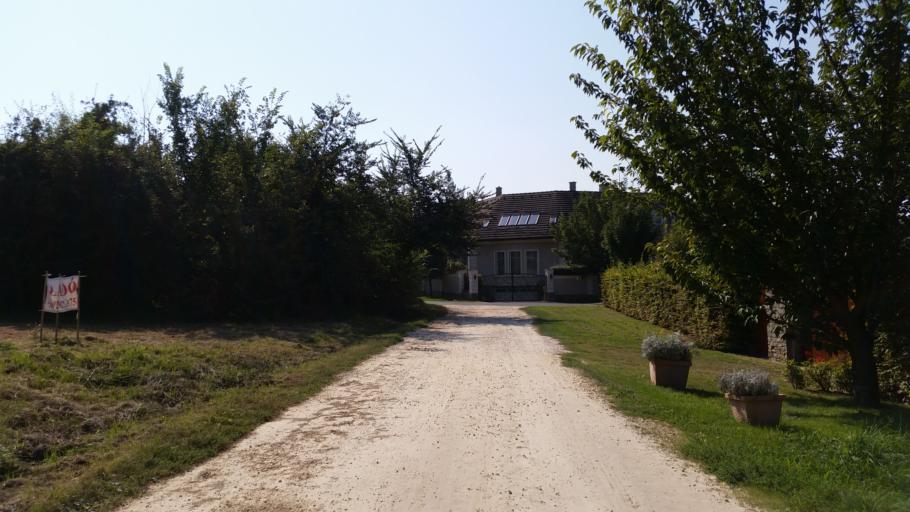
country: HU
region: Pest
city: Telki
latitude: 47.5536
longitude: 18.8257
